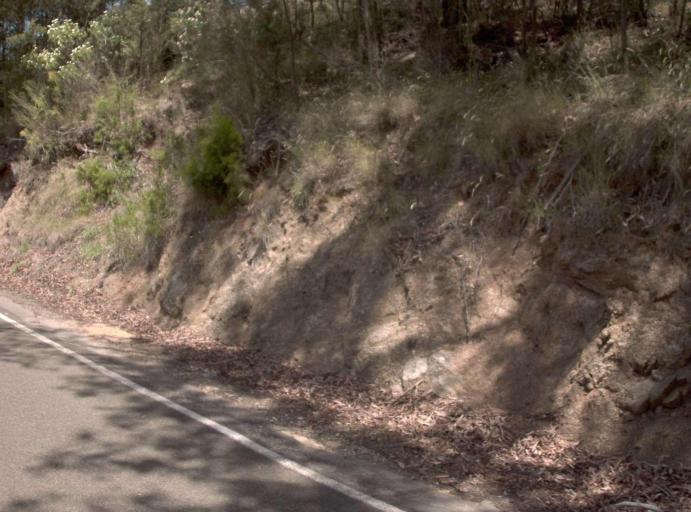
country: AU
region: Victoria
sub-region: East Gippsland
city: Bairnsdale
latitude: -37.4913
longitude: 147.8338
